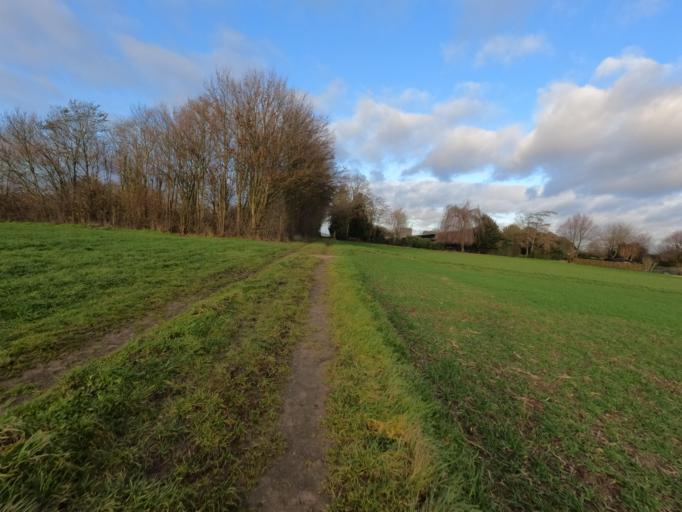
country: DE
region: North Rhine-Westphalia
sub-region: Regierungsbezirk Koln
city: Heinsberg
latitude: 51.0543
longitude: 6.0878
